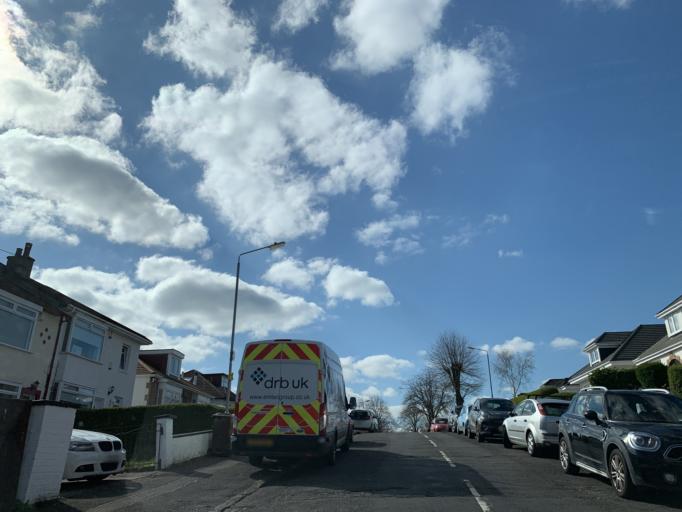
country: GB
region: Scotland
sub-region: East Renfrewshire
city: Clarkston
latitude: 55.7936
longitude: -4.2718
